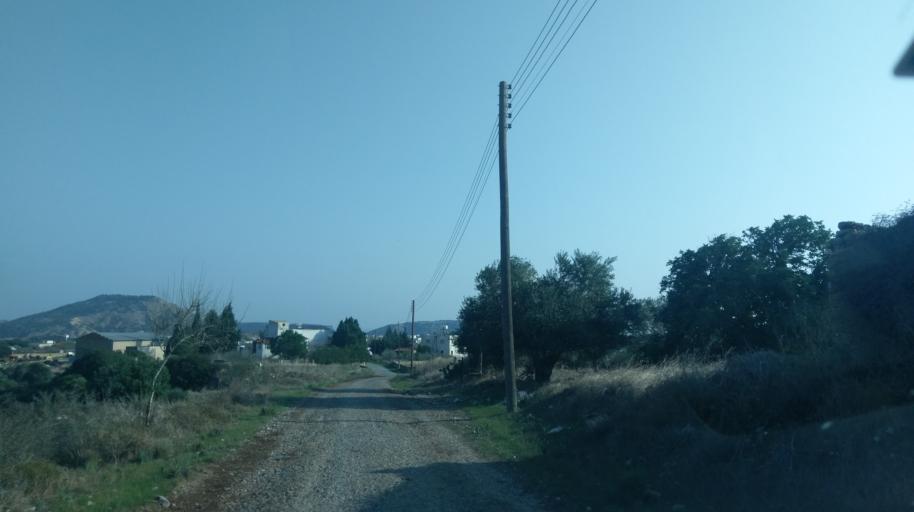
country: CY
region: Ammochostos
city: Rizokarpaso
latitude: 35.5164
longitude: 34.2690
